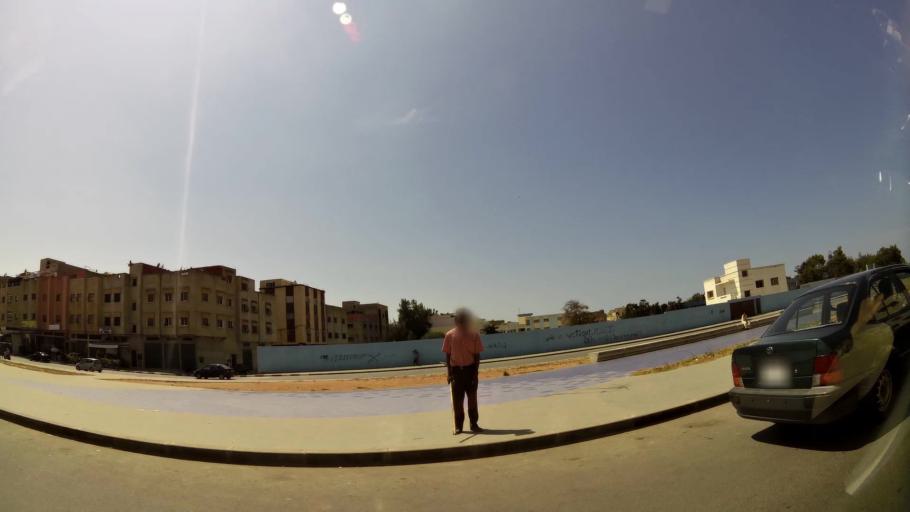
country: MA
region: Rabat-Sale-Zemmour-Zaer
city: Sale
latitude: 34.0654
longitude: -6.7796
